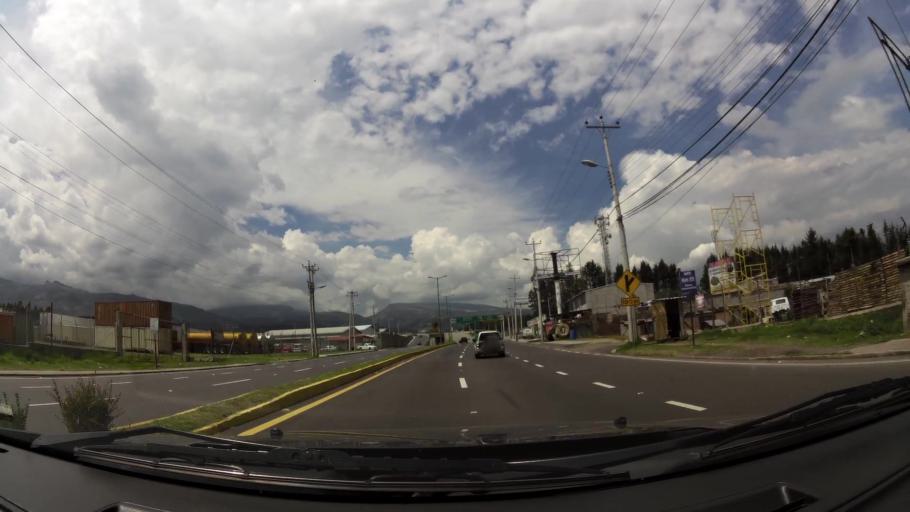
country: EC
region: Pichincha
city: Sangolqui
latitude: -0.2231
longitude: -78.3501
